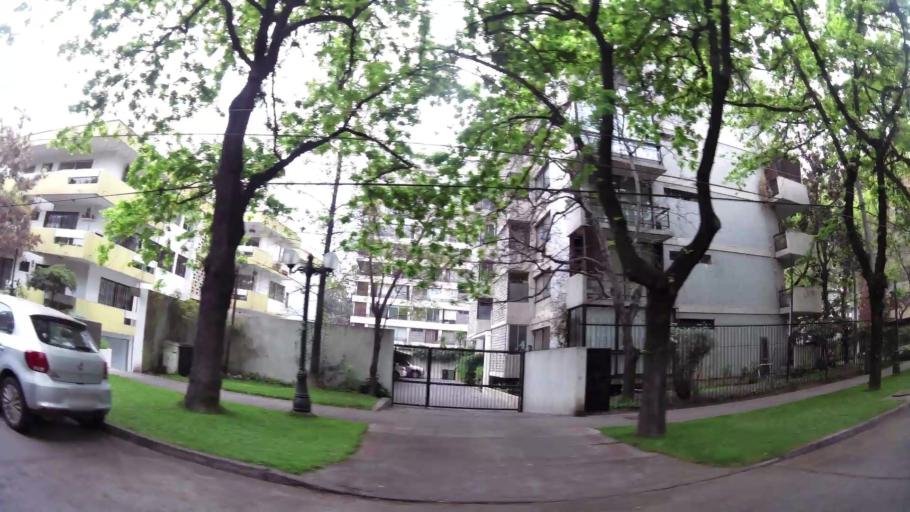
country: CL
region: Santiago Metropolitan
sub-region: Provincia de Santiago
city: Villa Presidente Frei, Nunoa, Santiago, Chile
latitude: -33.4242
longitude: -70.5997
